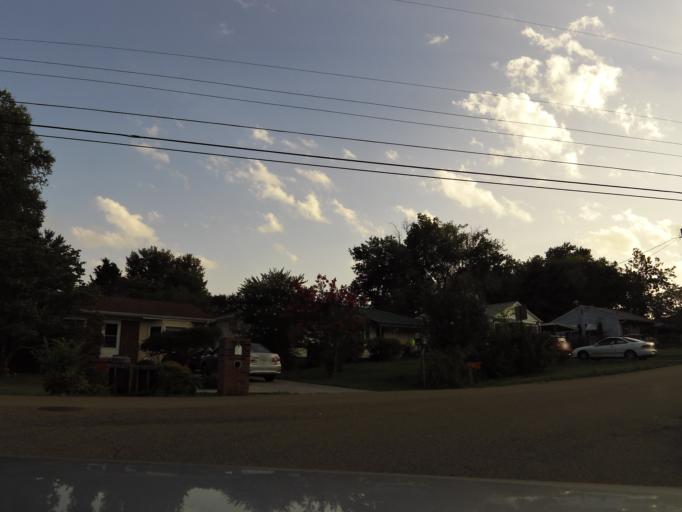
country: US
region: Tennessee
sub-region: Knox County
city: Knoxville
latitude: 35.9525
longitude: -83.8833
